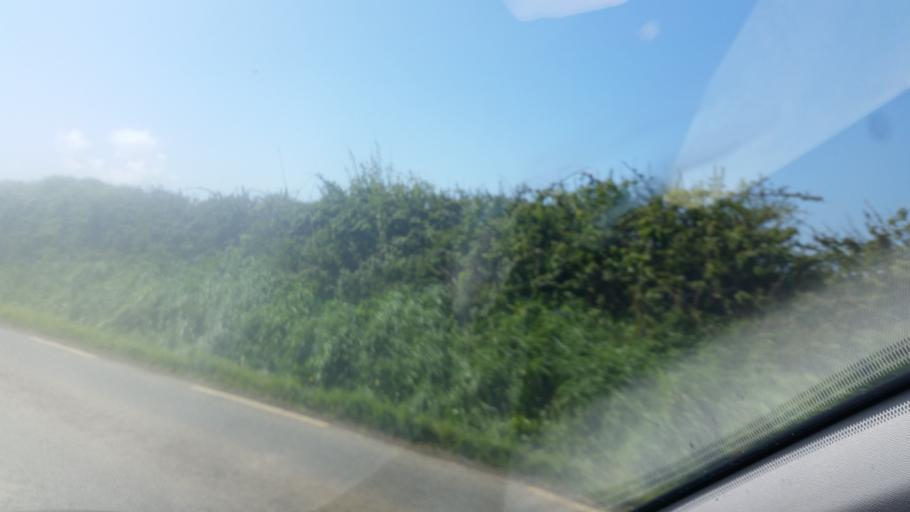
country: IE
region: Munster
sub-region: Waterford
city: Dunmore East
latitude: 52.2166
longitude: -6.8595
